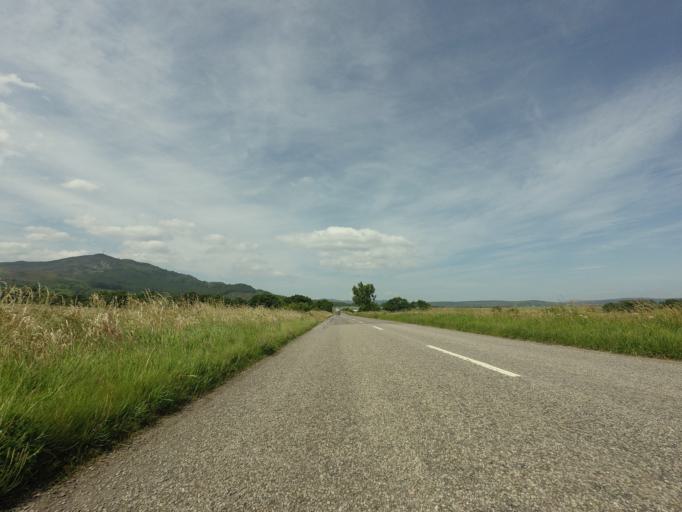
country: GB
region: Scotland
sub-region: Highland
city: Tain
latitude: 57.8417
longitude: -4.1949
